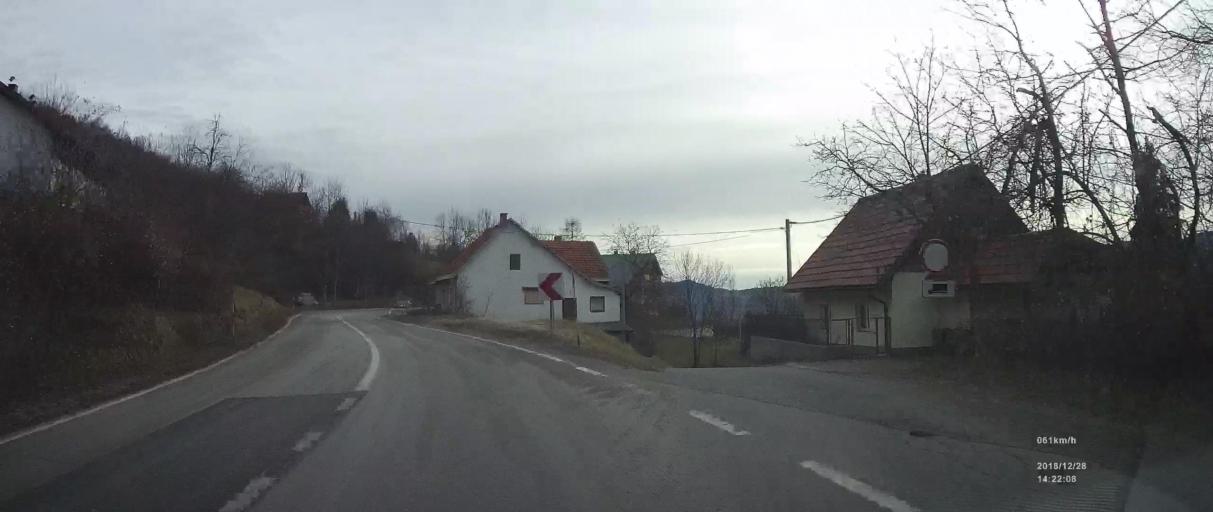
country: HR
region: Primorsko-Goranska
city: Vrbovsko
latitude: 45.3878
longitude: 15.0855
